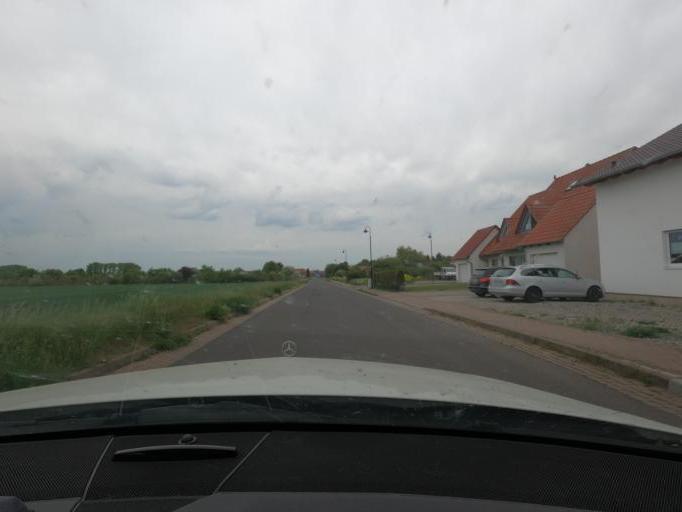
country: DE
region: Thuringia
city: Seebach
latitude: 51.1817
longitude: 10.4964
